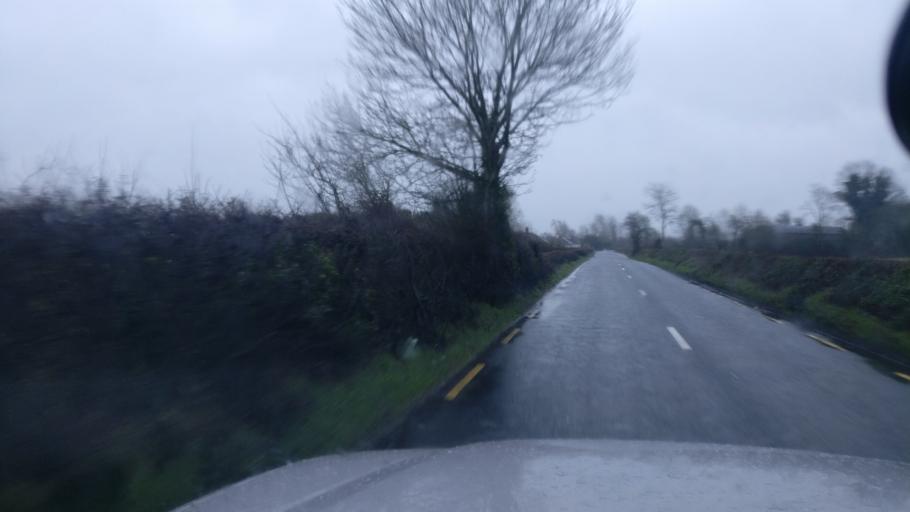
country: IE
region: Connaught
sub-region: County Galway
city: Ballinasloe
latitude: 53.2780
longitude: -8.2128
